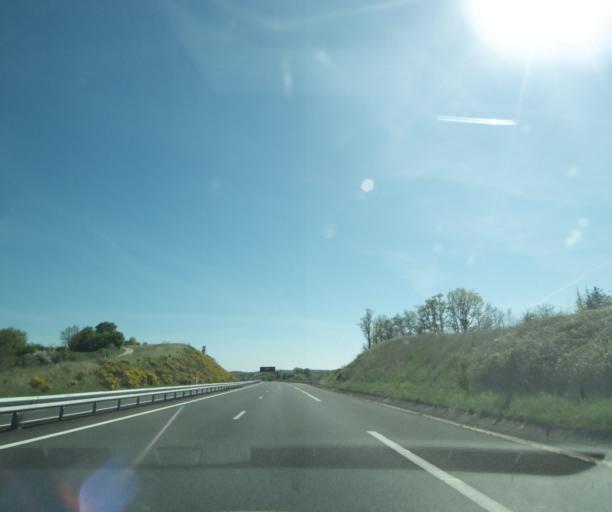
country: FR
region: Midi-Pyrenees
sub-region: Departement du Lot
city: Pradines
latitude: 44.5686
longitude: 1.5121
